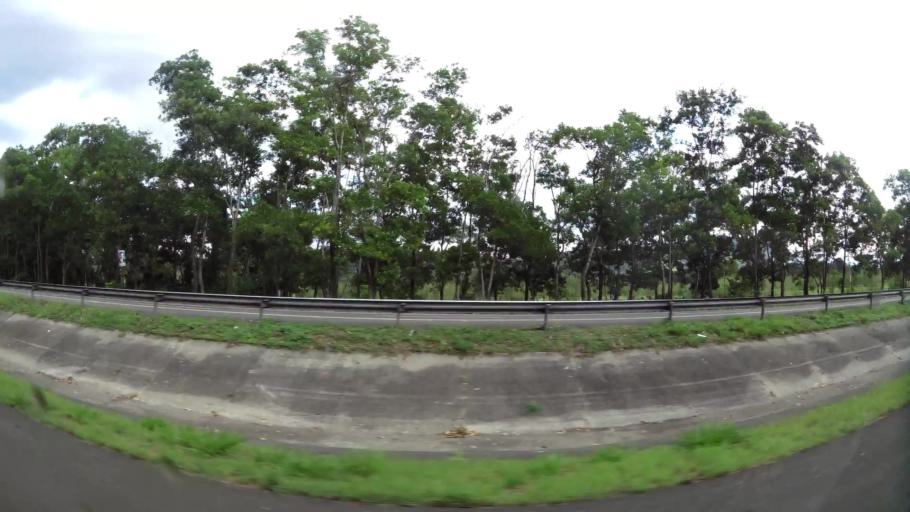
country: DO
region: Monsenor Nouel
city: Bonao
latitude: 18.9190
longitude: -70.3808
